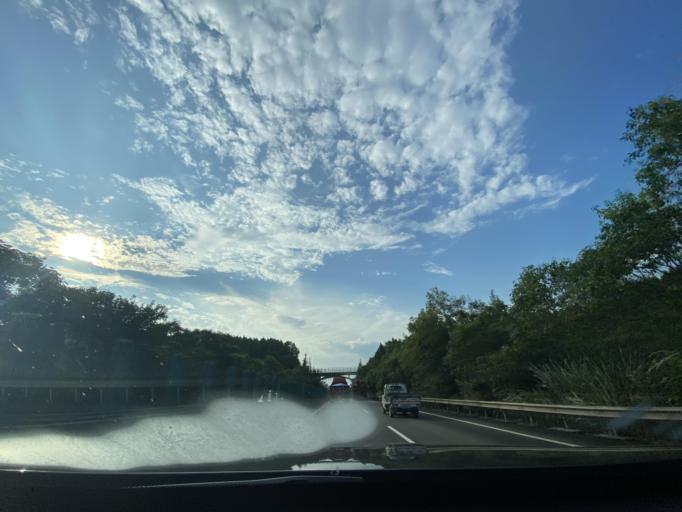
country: CN
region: Sichuan
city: Jiancheng
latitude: 30.3262
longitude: 104.5699
